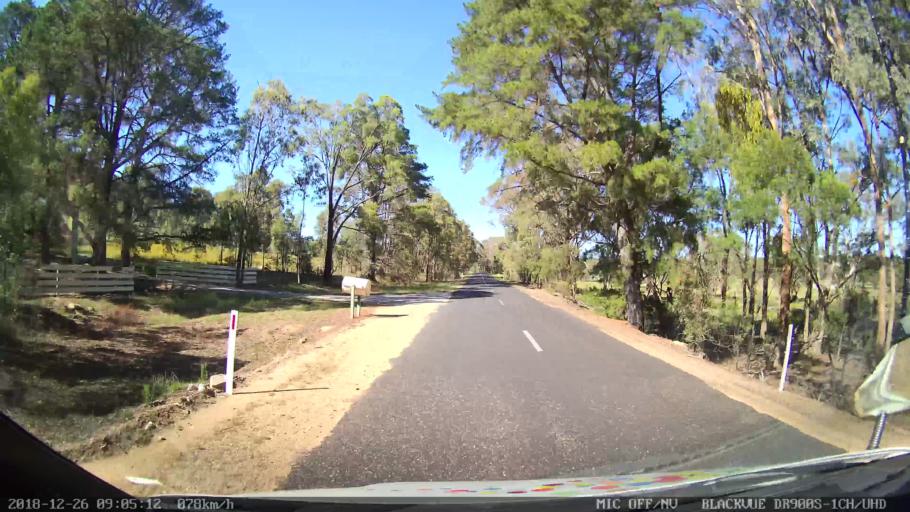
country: AU
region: New South Wales
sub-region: Mid-Western Regional
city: Kandos
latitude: -32.6805
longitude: 150.0099
